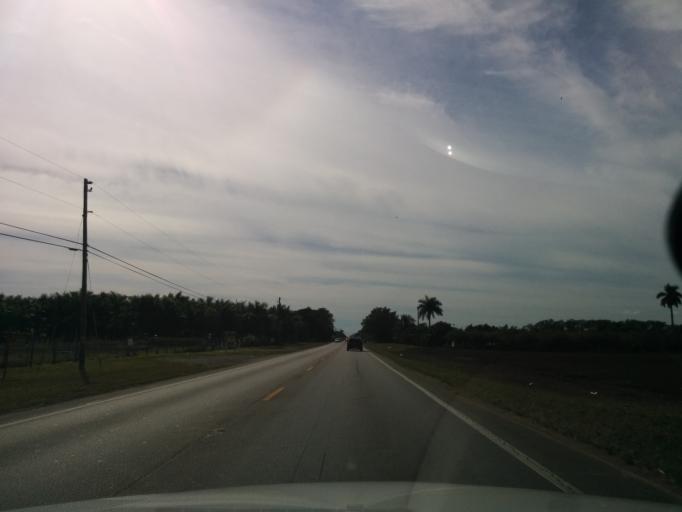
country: US
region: Florida
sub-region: Miami-Dade County
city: Homestead
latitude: 25.5101
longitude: -80.4778
